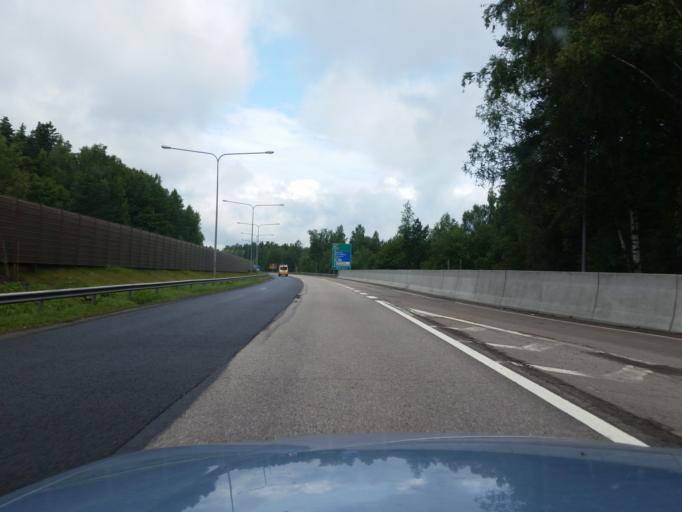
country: FI
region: Uusimaa
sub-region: Helsinki
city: Espoo
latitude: 60.2396
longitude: 24.5777
